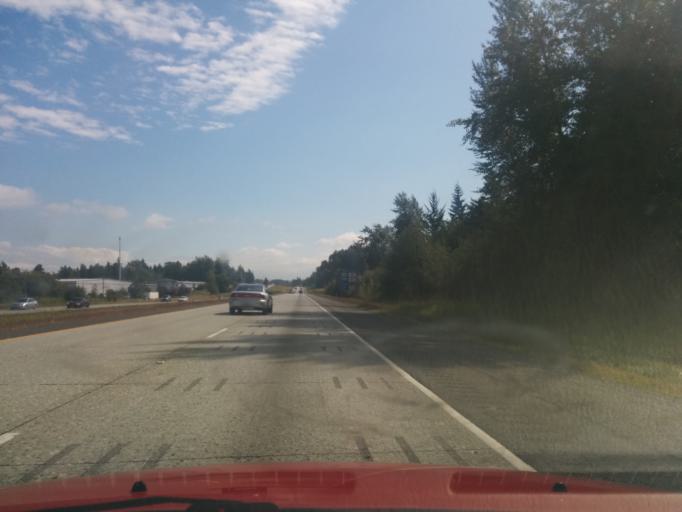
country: US
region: Washington
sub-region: Whatcom County
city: Marietta-Alderwood
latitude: 48.8014
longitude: -122.5331
